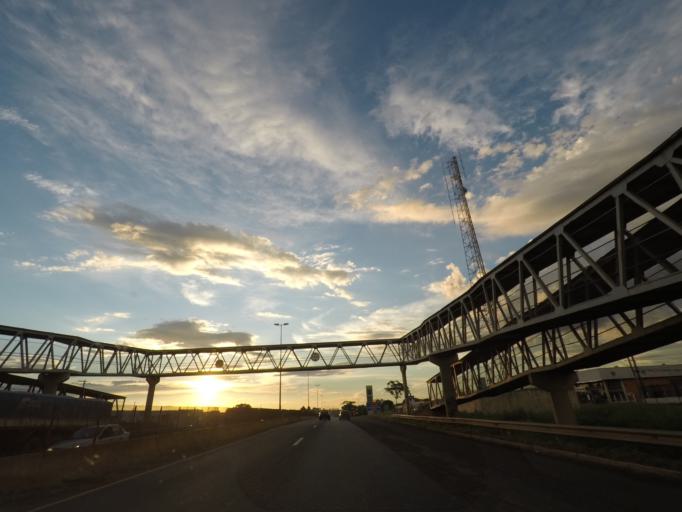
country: BR
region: Minas Gerais
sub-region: Uberaba
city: Uberaba
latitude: -19.7780
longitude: -47.9277
